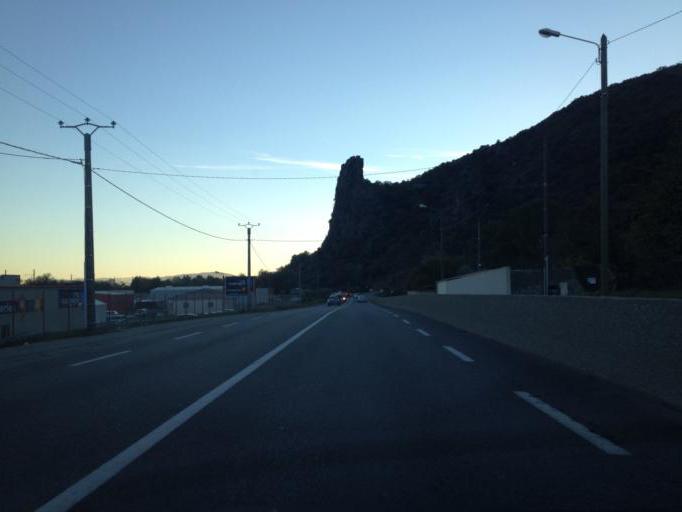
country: FR
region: Rhone-Alpes
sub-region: Departement de l'Ardeche
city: Meysse
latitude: 44.5994
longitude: 4.7164
